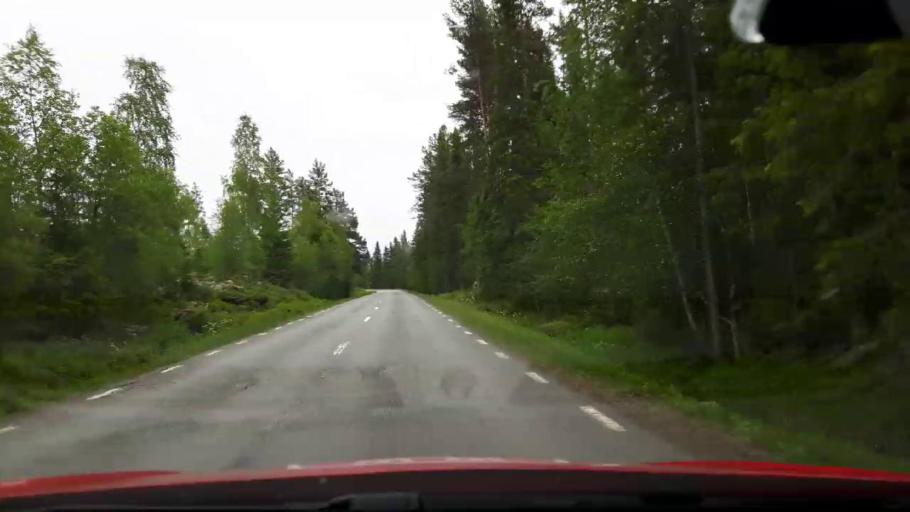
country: SE
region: Jaemtland
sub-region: Stroemsunds Kommun
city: Stroemsund
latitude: 63.4254
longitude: 15.5136
